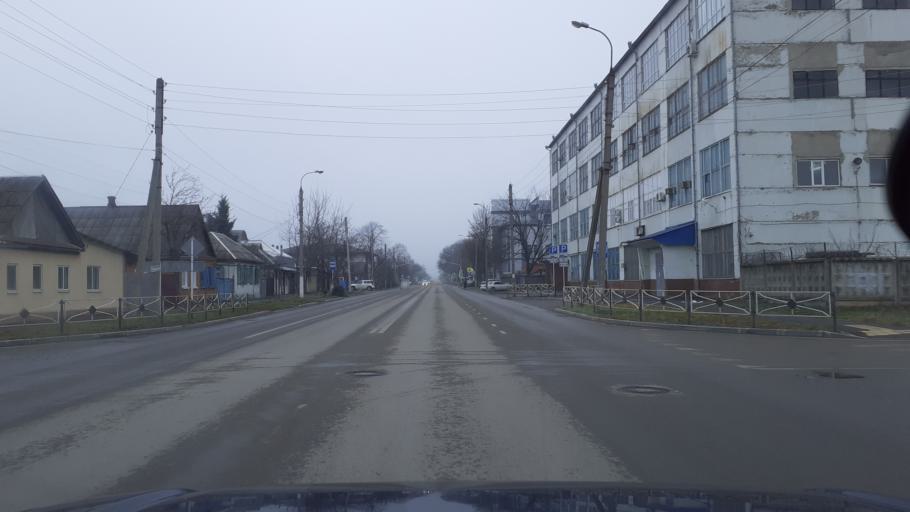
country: RU
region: Adygeya
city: Maykop
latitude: 44.6146
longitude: 40.0867
